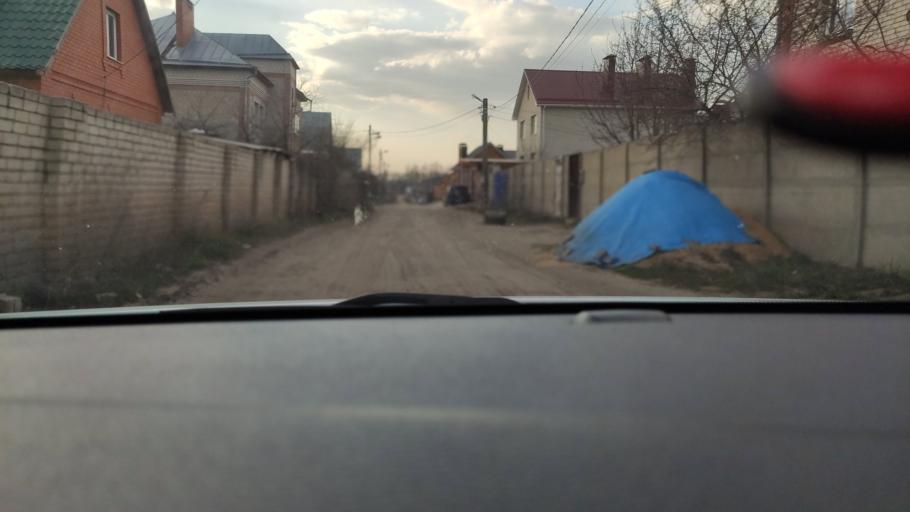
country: RU
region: Voronezj
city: Pridonskoy
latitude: 51.6367
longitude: 39.0951
